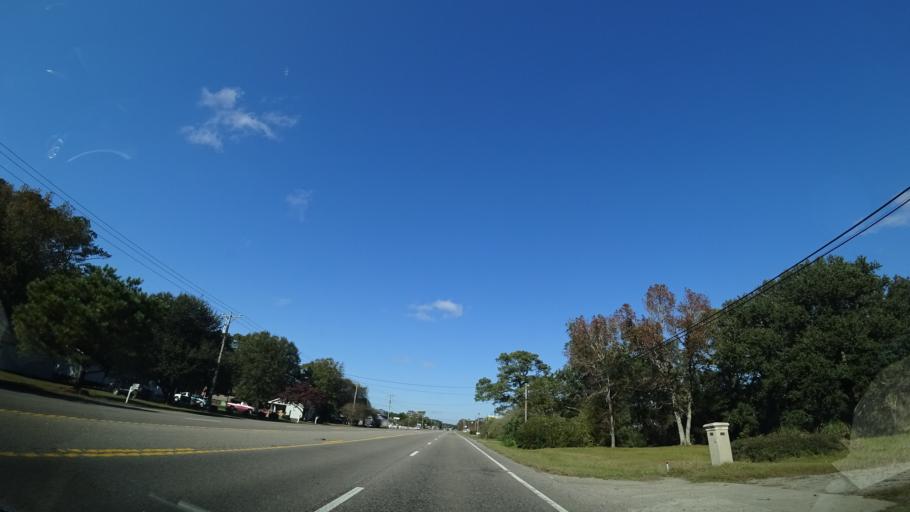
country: US
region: North Carolina
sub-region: Dare County
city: Southern Shores
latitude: 36.1665
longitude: -75.8590
